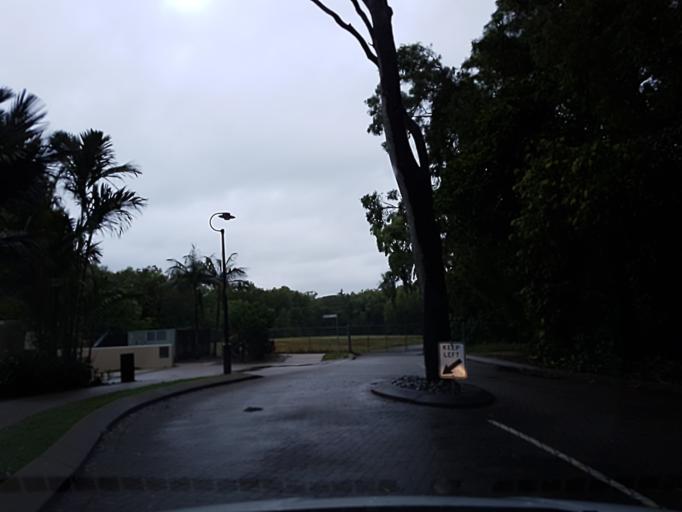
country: AU
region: Queensland
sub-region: Cairns
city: Palm Cove
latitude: -16.7532
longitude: 145.6701
